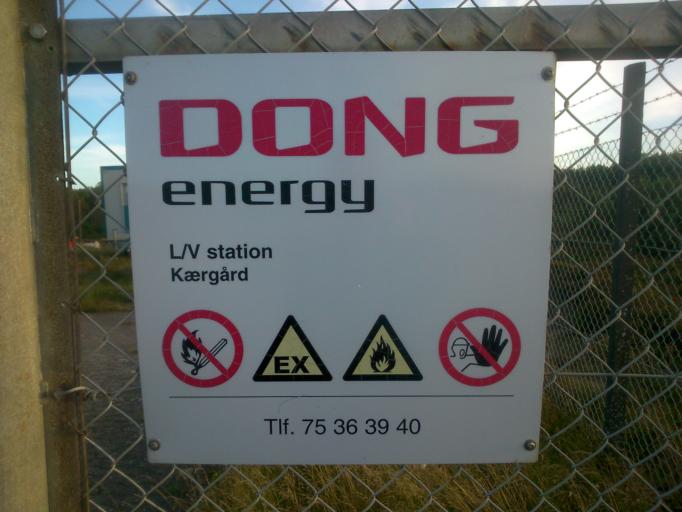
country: DK
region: South Denmark
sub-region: Varde Kommune
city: Oksbol
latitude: 55.6900
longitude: 8.1598
